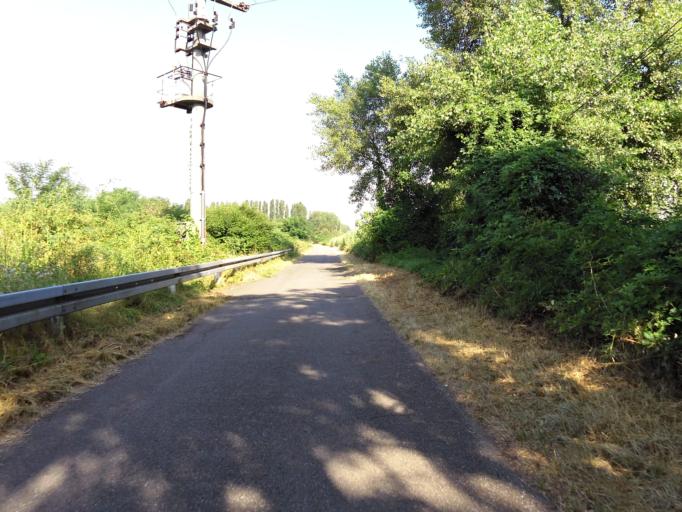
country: DE
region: Baden-Wuerttemberg
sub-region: Karlsruhe Region
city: Mannheim
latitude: 49.5364
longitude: 8.4428
